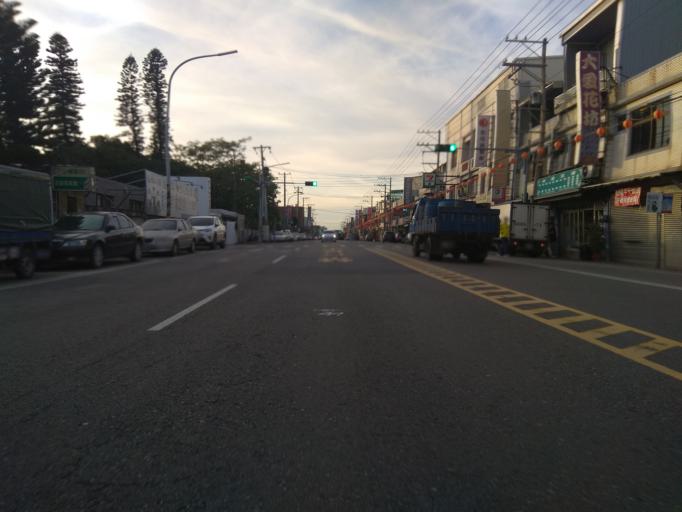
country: TW
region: Taiwan
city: Taoyuan City
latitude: 24.9940
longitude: 121.1667
